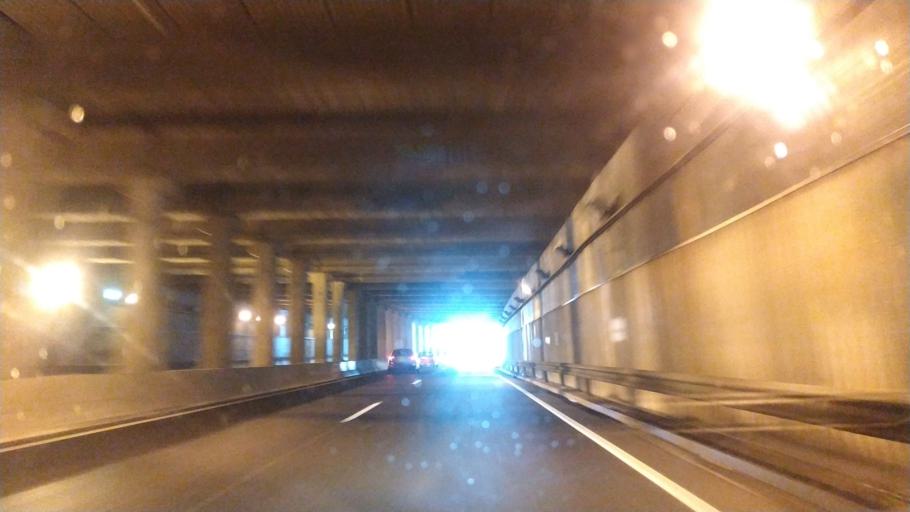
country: ES
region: Galicia
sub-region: Provincia da Coruna
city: A Coruna
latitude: 43.3523
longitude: -8.3907
